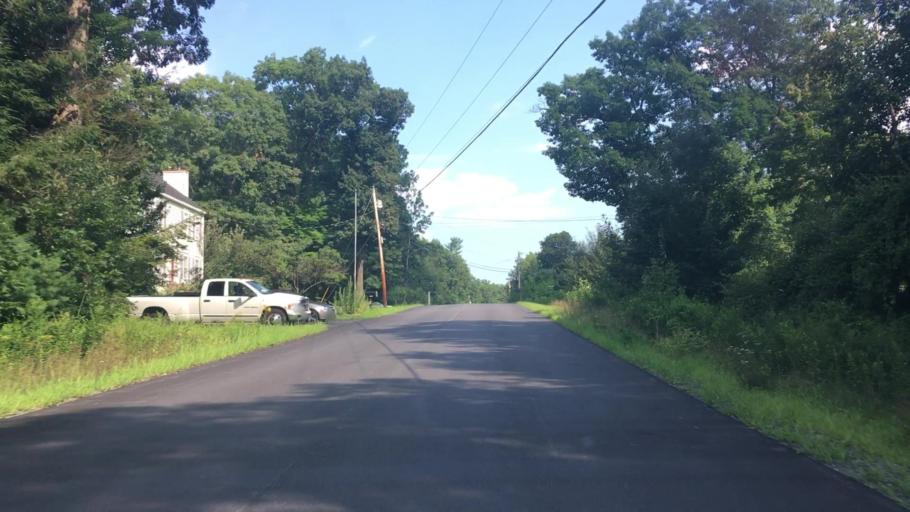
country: US
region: New Hampshire
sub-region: Rockingham County
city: Derry Village
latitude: 42.9384
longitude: -71.3293
